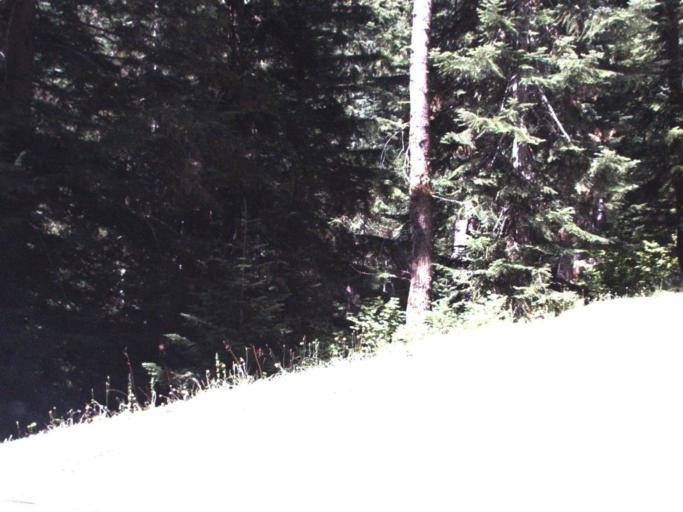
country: US
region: Washington
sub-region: King County
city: Enumclaw
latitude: 46.8025
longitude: -121.5550
